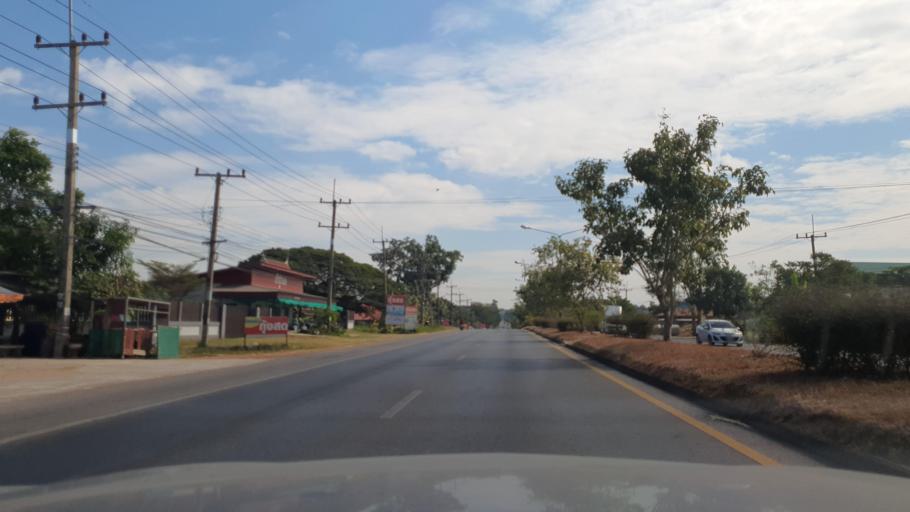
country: TH
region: Kalasin
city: Yang Talat
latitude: 16.4073
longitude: 103.4051
